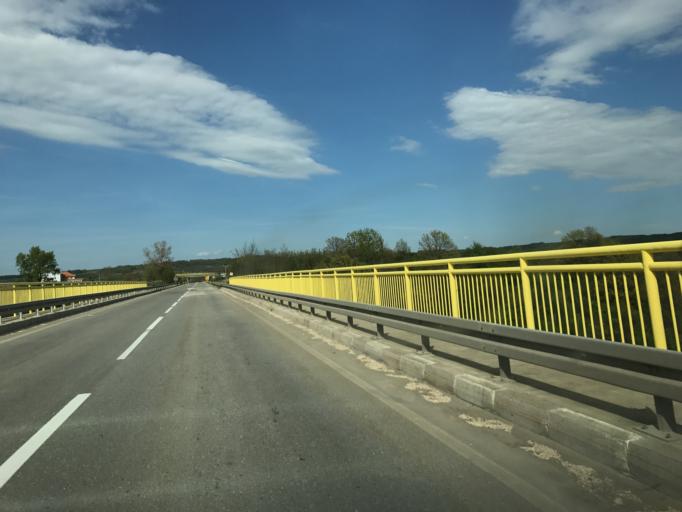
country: RS
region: Central Serbia
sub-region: Zajecarski Okrug
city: Zajecar
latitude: 44.0873
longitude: 22.3406
